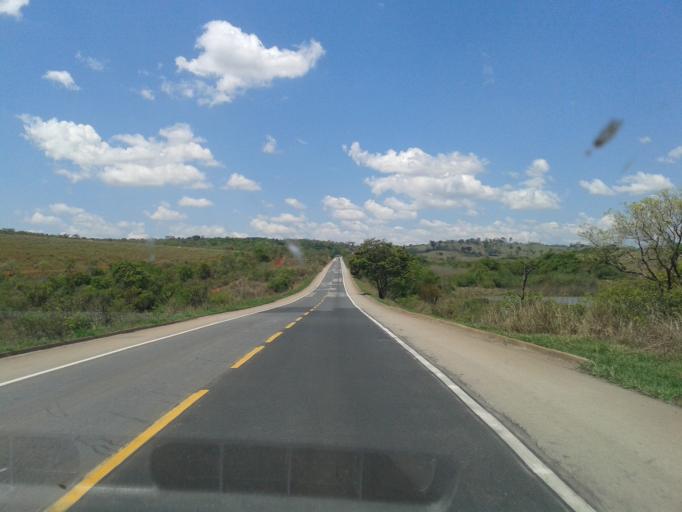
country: BR
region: Minas Gerais
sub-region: Ibia
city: Ibia
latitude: -19.5677
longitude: -46.6480
